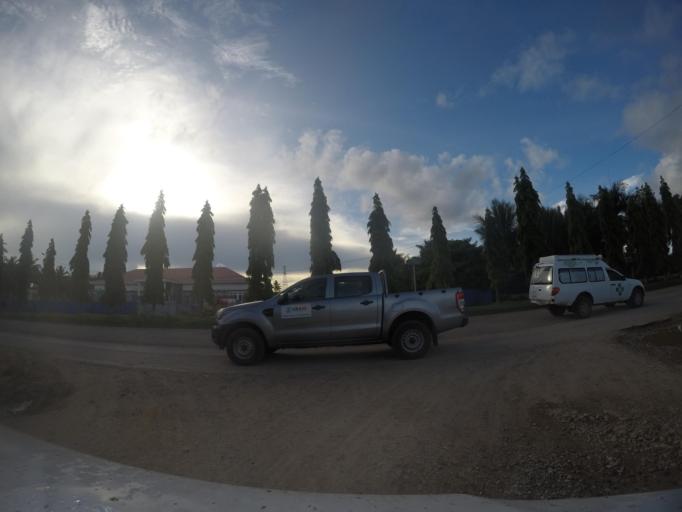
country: TL
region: Lautem
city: Lospalos
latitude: -8.4959
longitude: 126.9920
